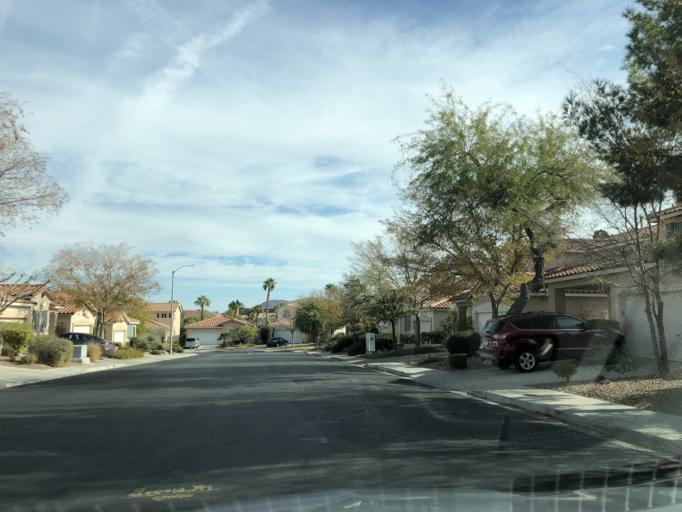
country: US
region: Nevada
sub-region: Clark County
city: Whitney
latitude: 36.0152
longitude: -115.0847
